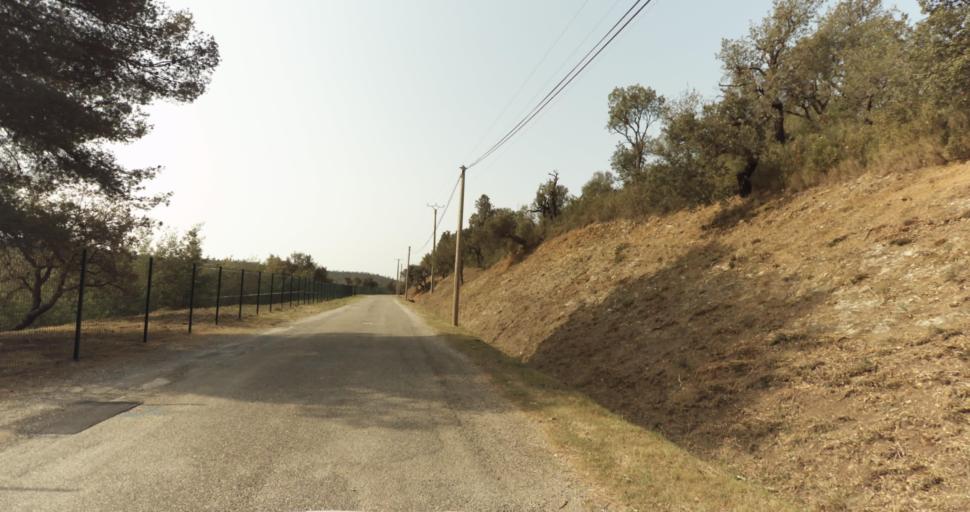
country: FR
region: Provence-Alpes-Cote d'Azur
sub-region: Departement du Var
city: Bormes-les-Mimosas
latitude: 43.1441
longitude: 6.2928
